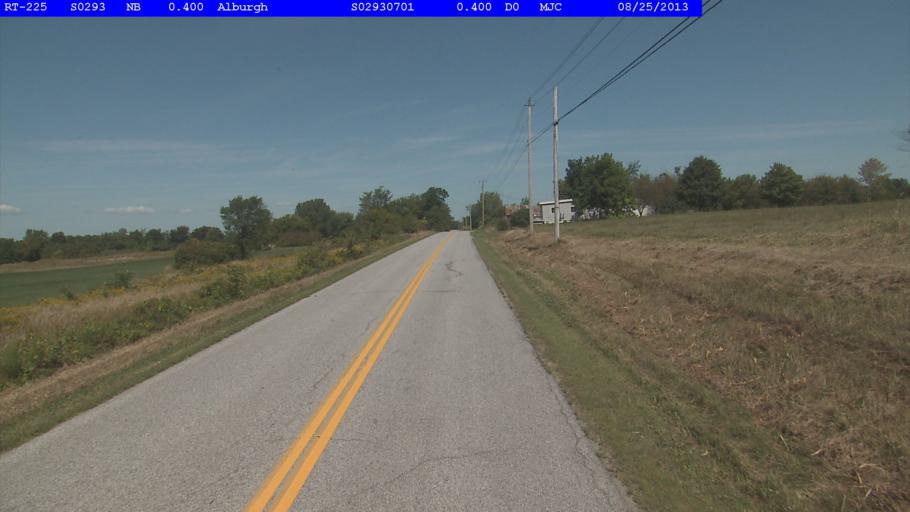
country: US
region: New York
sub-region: Clinton County
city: Rouses Point
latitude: 44.9945
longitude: -73.2960
